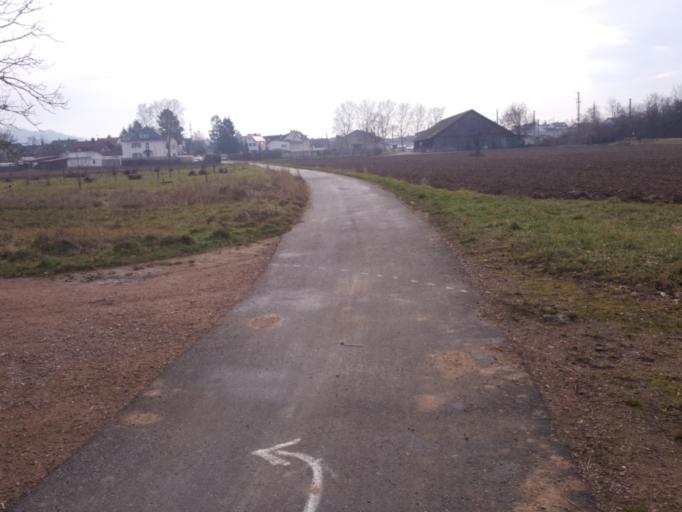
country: DE
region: Baden-Wuerttemberg
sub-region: Freiburg Region
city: Eimeldingen
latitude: 47.6210
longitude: 7.6056
